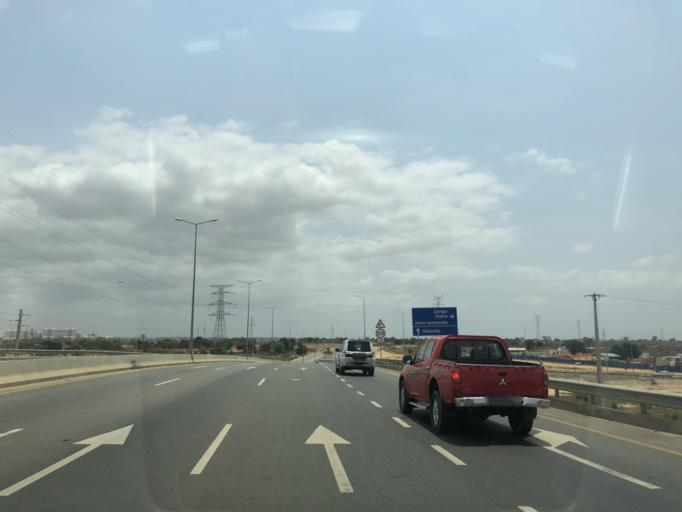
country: AO
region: Luanda
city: Luanda
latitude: -8.9738
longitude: 13.2538
